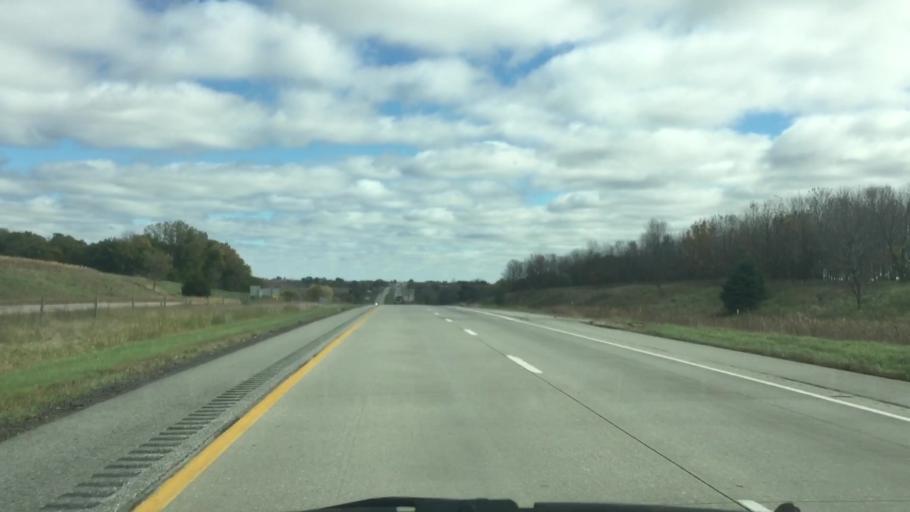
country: US
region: Iowa
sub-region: Jasper County
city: Newton
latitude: 41.6823
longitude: -92.9952
